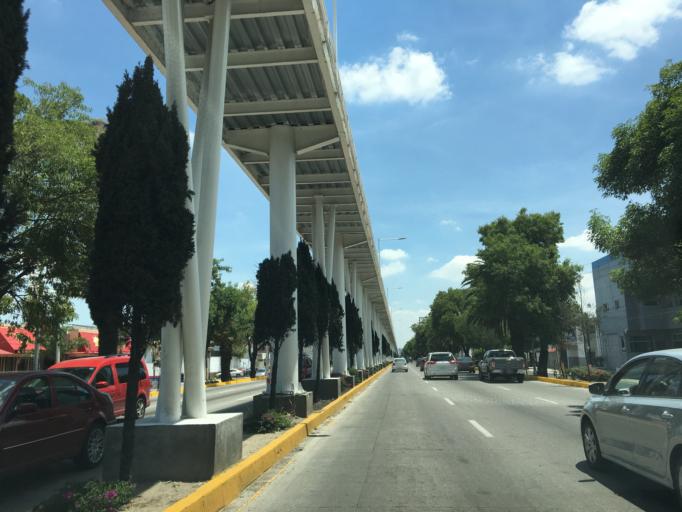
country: MX
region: Puebla
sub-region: Cuautlancingo
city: Sanctorum
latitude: 19.0803
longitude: -98.2283
